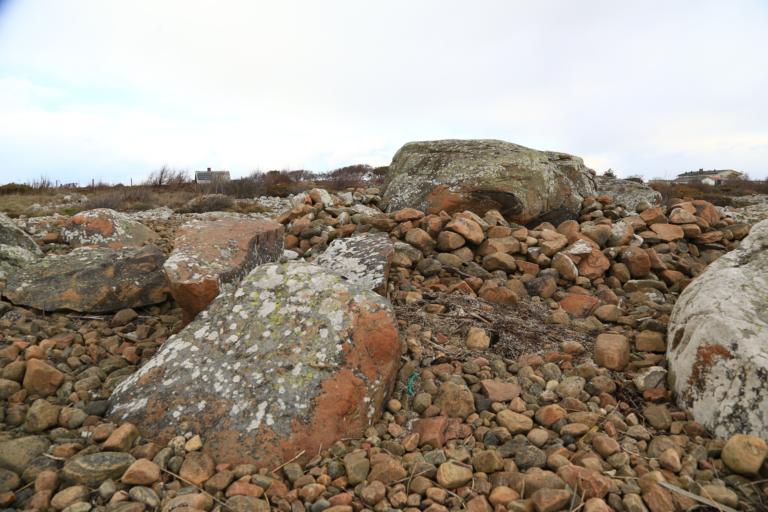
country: SE
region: Halland
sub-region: Varbergs Kommun
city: Traslovslage
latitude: 57.0486
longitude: 12.2741
